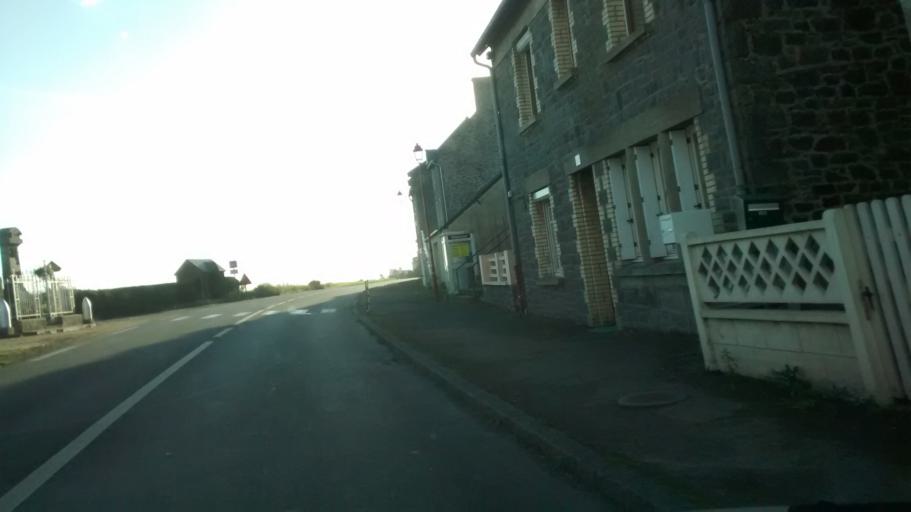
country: FR
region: Brittany
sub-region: Departement d'Ille-et-Vilaine
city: La Fresnais
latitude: 48.6139
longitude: -1.8411
